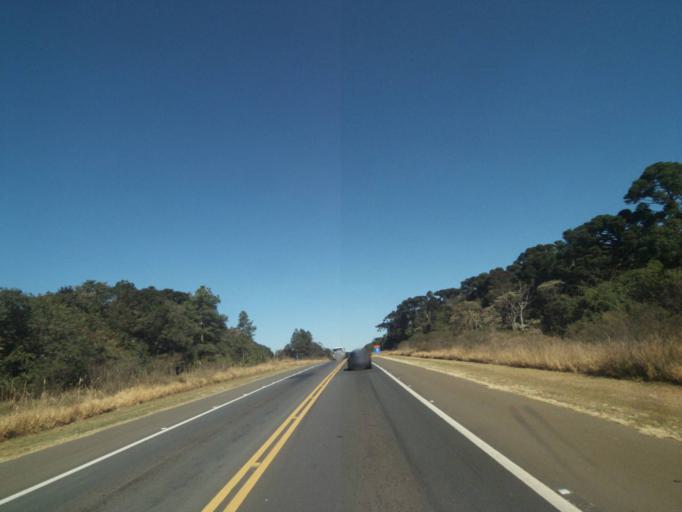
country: BR
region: Parana
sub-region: Tibagi
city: Tibagi
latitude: -24.7255
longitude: -50.5383
